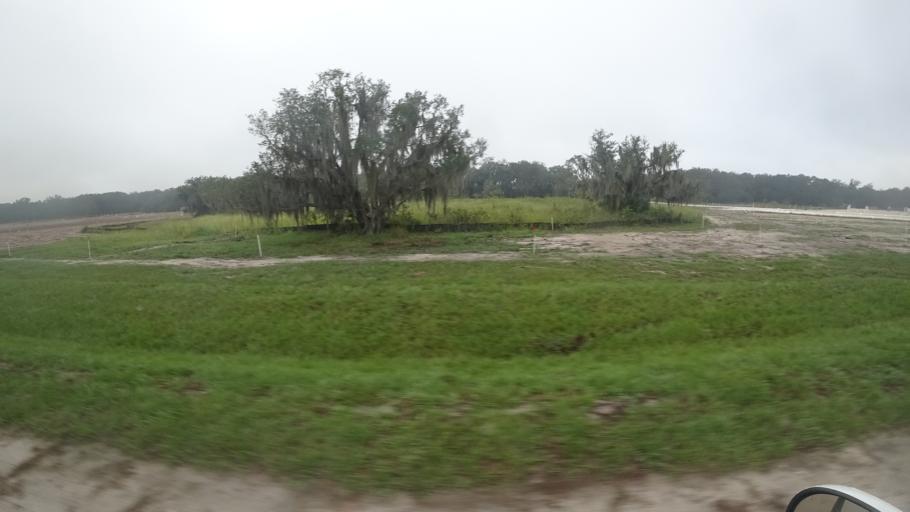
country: US
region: Florida
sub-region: Sarasota County
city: Lake Sarasota
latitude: 27.2920
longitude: -82.2182
